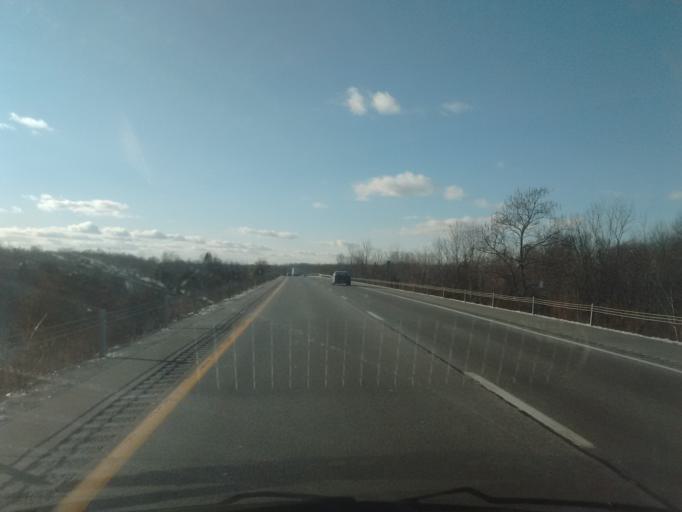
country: US
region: New York
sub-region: Orange County
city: Walden
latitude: 41.5179
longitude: -74.1856
